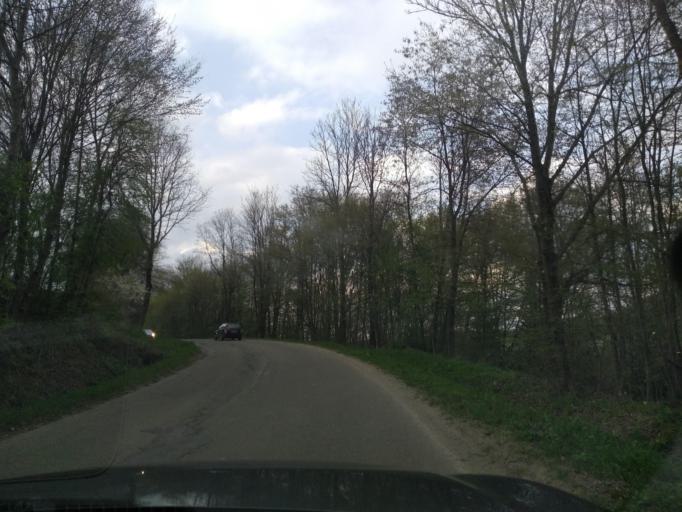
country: PL
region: Subcarpathian Voivodeship
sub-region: Powiat sanocki
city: Czaszyn
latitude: 49.4125
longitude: 22.2331
